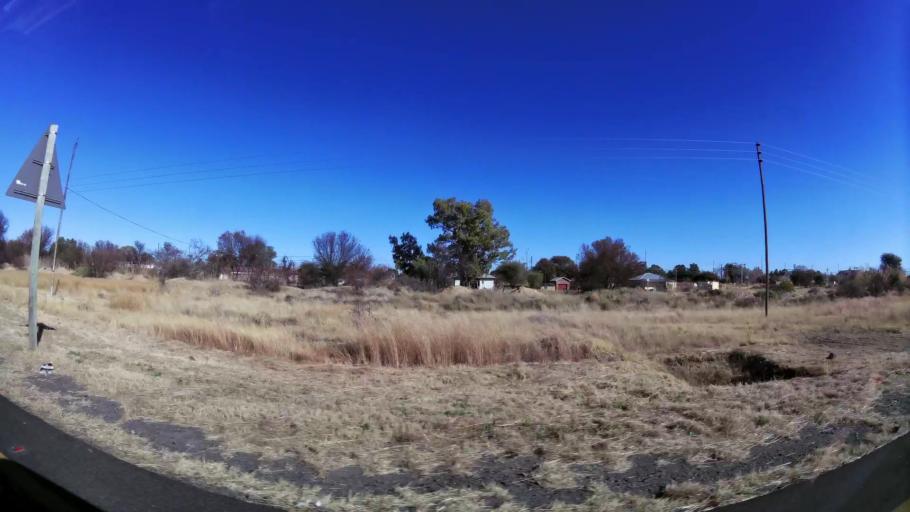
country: ZA
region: Northern Cape
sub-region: Frances Baard District Municipality
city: Kimberley
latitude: -28.6937
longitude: 24.7780
